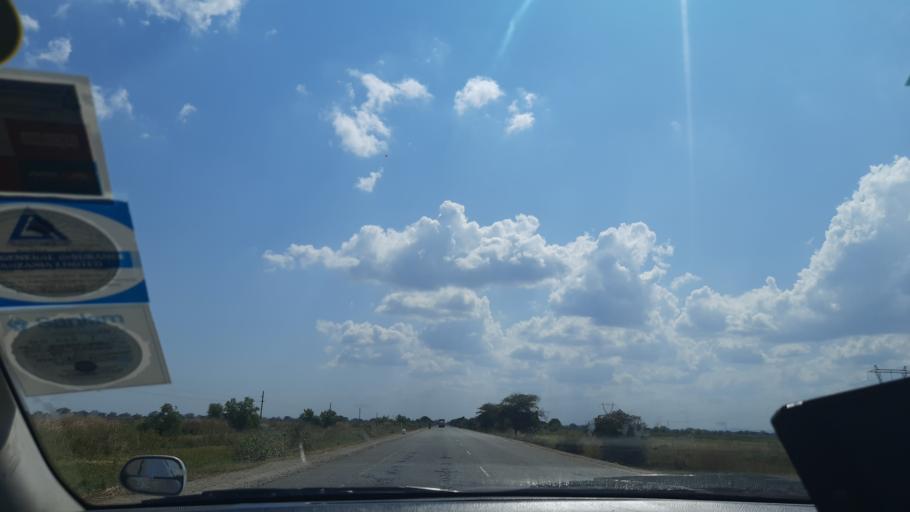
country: TZ
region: Singida
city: Kintinku
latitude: -5.9421
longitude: 35.2984
